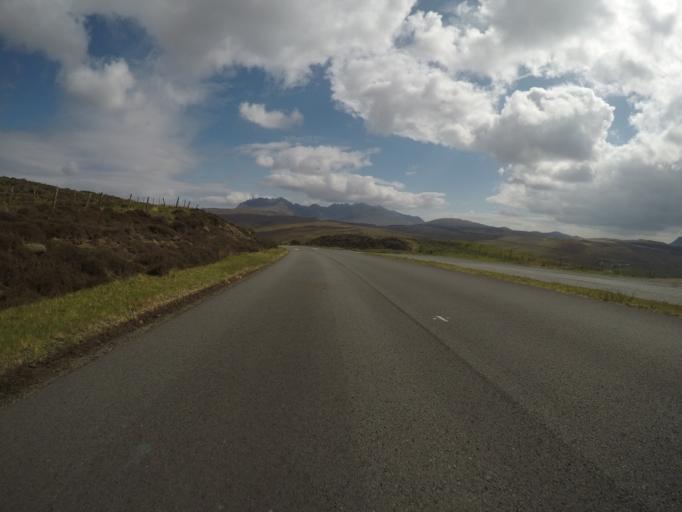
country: GB
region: Scotland
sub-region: Highland
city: Isle of Skye
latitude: 57.3062
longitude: -6.3147
